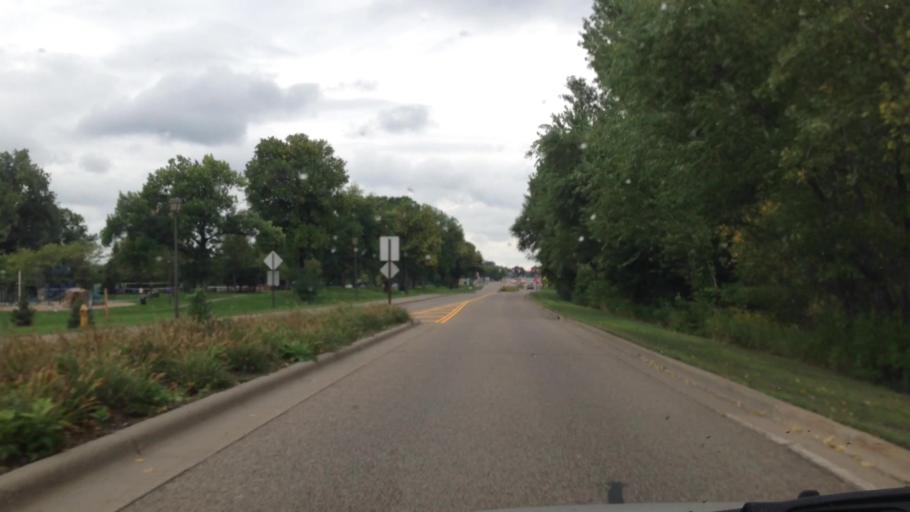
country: US
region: Minnesota
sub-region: Hennepin County
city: Golden Valley
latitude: 44.9791
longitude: -93.3802
